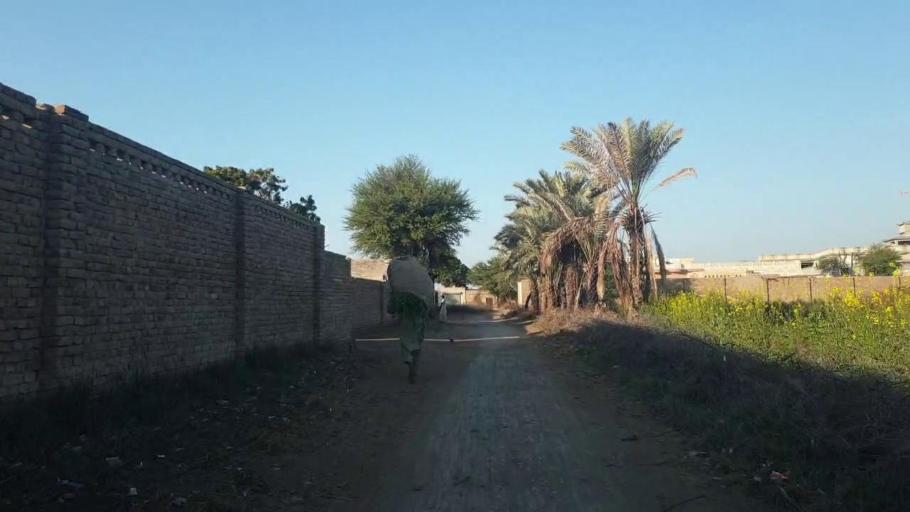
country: PK
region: Sindh
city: Shahpur Chakar
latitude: 26.0694
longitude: 68.6400
